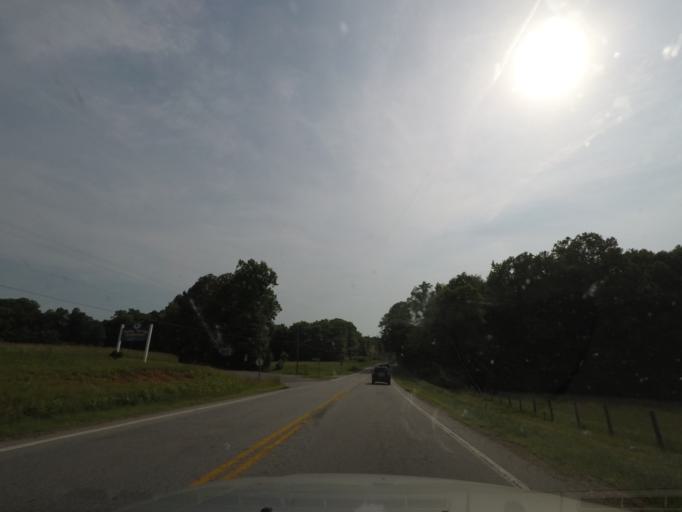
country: US
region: Virginia
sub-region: Prince Edward County
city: Hampden Sydney
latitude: 37.2545
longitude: -78.4185
